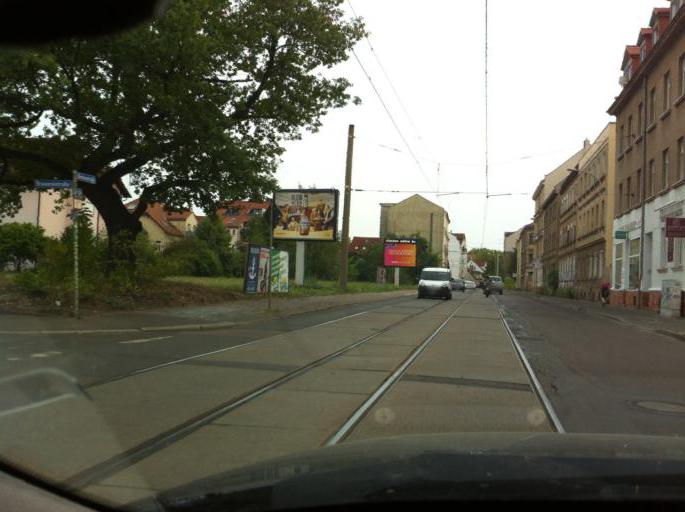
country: DE
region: Saxony
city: Markkleeberg
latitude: 51.3039
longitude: 12.3276
